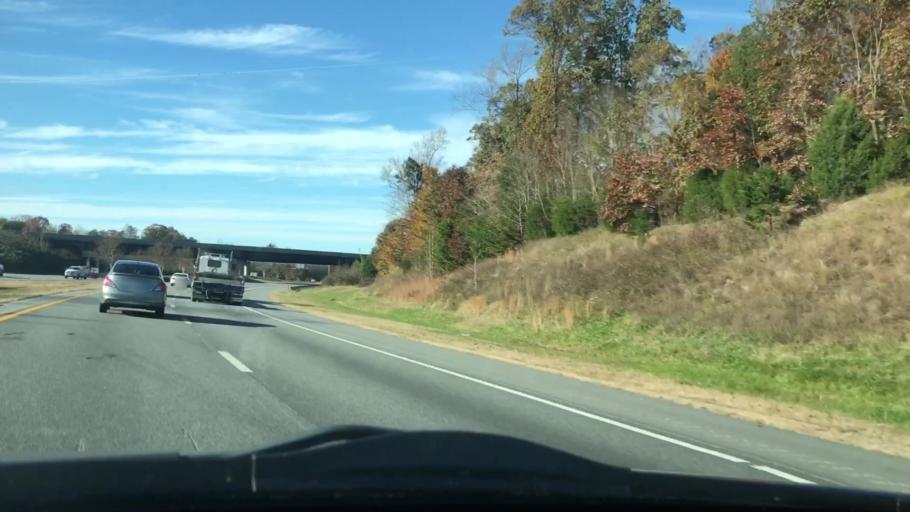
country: US
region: North Carolina
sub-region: Guilford County
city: High Point
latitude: 36.0082
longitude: -80.0327
